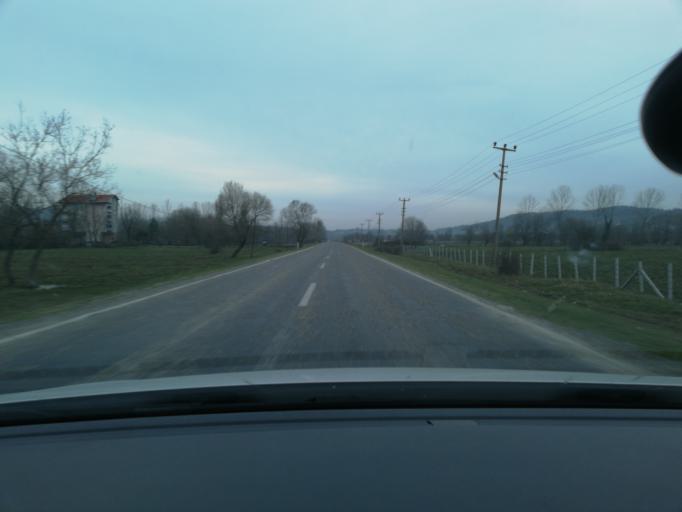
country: TR
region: Zonguldak
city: Saltukova
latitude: 41.5062
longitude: 32.0997
